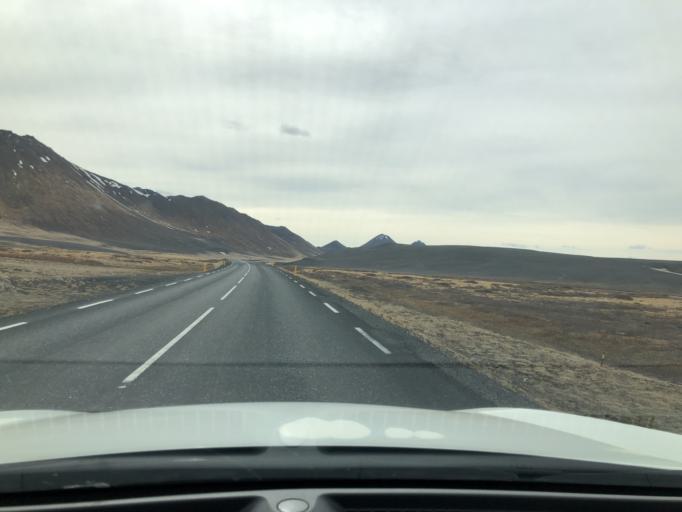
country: IS
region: Northeast
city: Laugar
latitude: 65.4864
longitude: -15.9656
